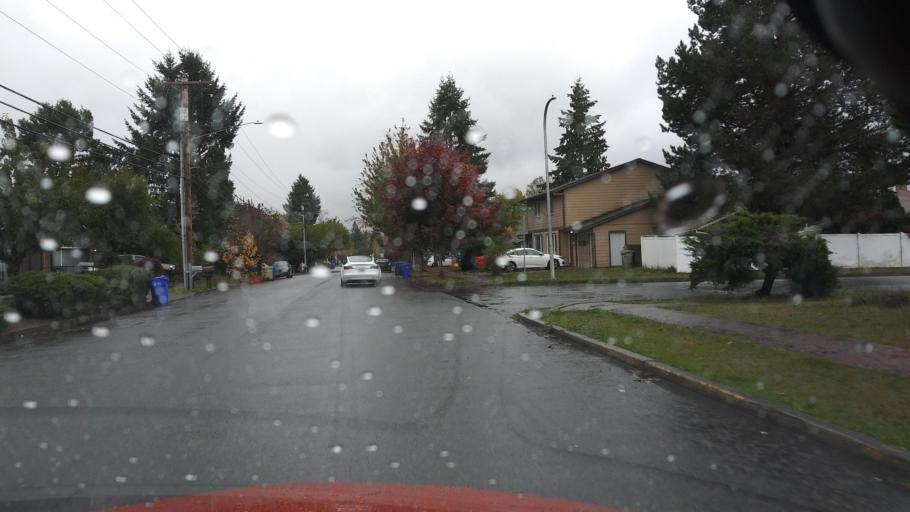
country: US
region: Oregon
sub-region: Washington County
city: Cornelius
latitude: 45.5181
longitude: -123.0669
